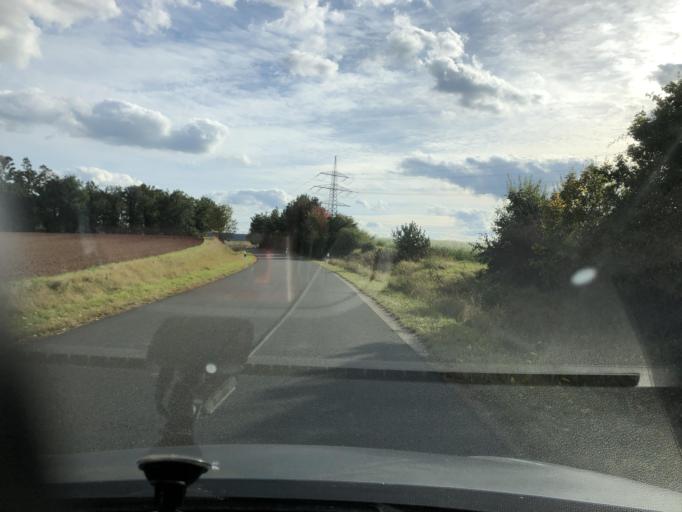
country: DE
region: Bavaria
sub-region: Regierungsbezirk Mittelfranken
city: Cadolzburg
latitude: 49.4843
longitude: 10.8289
